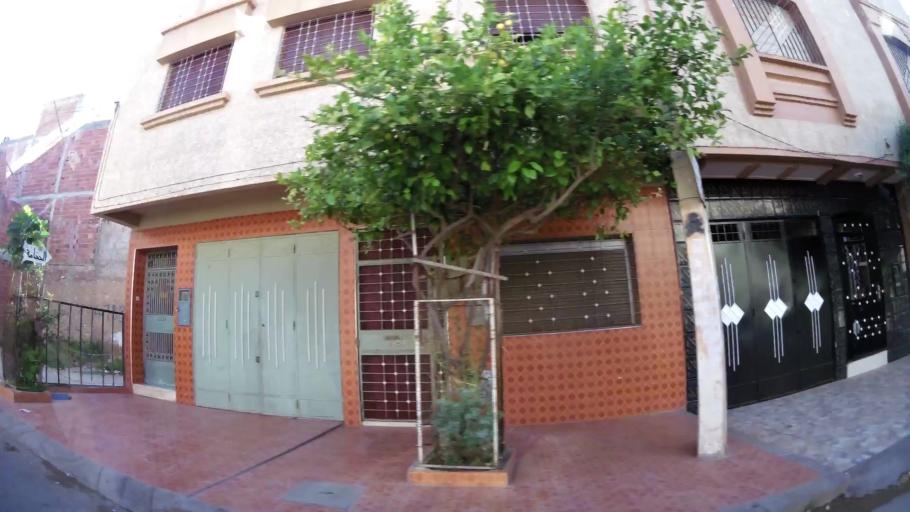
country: MA
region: Oriental
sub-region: Oujda-Angad
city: Oujda
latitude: 34.6698
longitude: -1.8959
